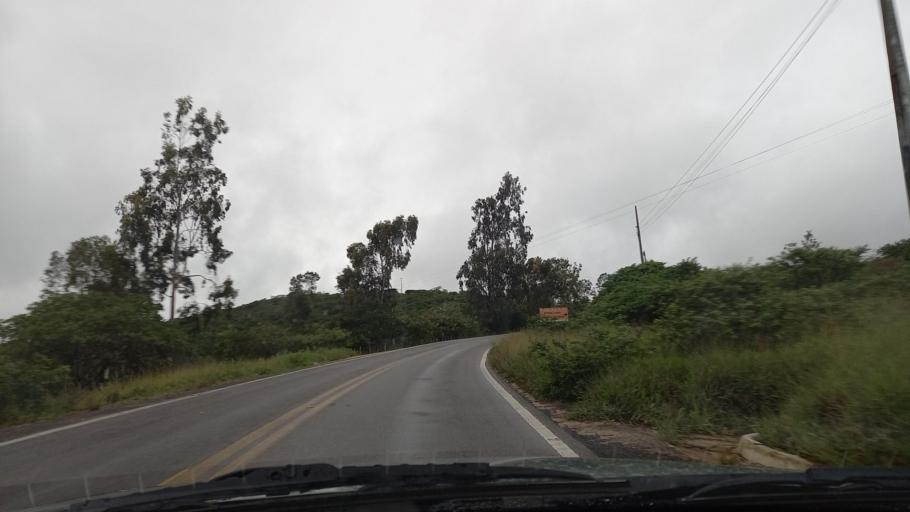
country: BR
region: Pernambuco
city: Garanhuns
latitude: -8.8499
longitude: -36.5157
